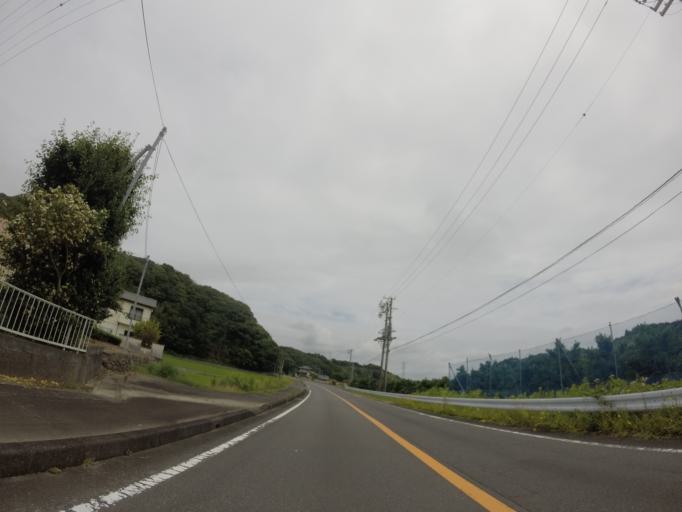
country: JP
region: Shizuoka
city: Shimada
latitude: 34.7835
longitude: 138.1580
